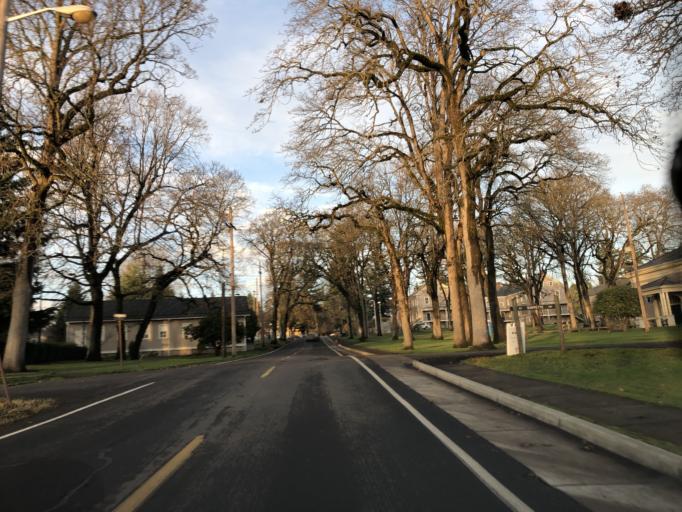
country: US
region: Washington
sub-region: Clark County
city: Vancouver
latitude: 45.6258
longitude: -122.6653
